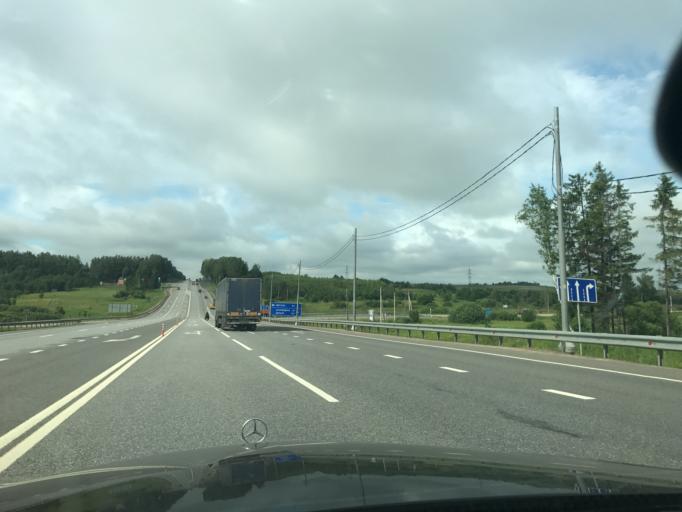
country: RU
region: Smolensk
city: Kardymovo
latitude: 55.0154
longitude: 32.2977
